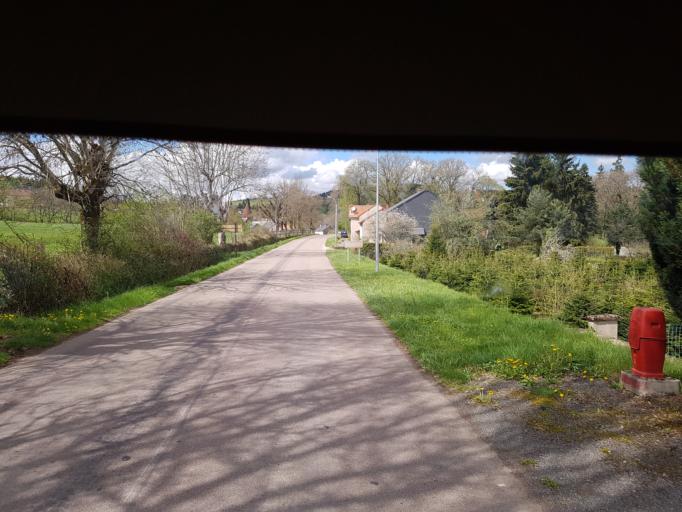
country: FR
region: Bourgogne
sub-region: Departement de la Cote-d'Or
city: Saulieu
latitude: 47.1122
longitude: 4.2274
